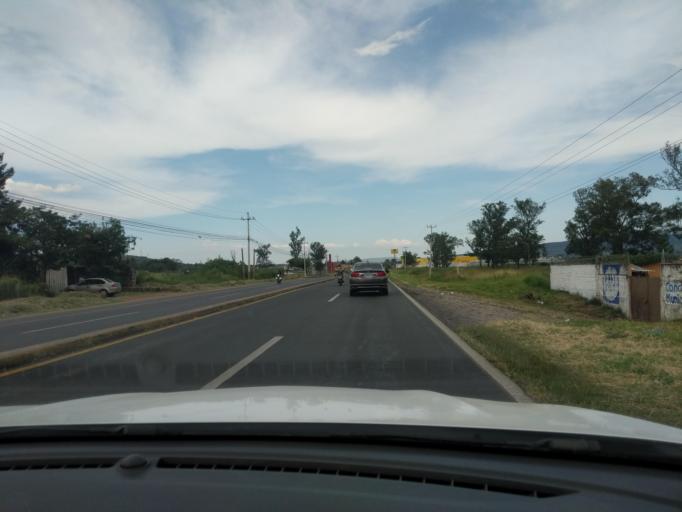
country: MX
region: Jalisco
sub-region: El Salto
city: Galaxia Bonito Jalisco
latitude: 20.5055
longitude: -103.2110
